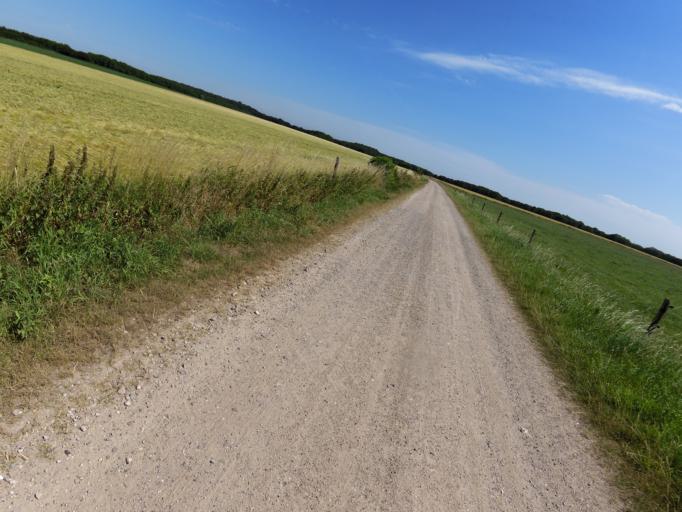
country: NL
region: Limburg
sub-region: Valkenburg aan de Geul
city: Sibbe
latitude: 50.8380
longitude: 5.8393
